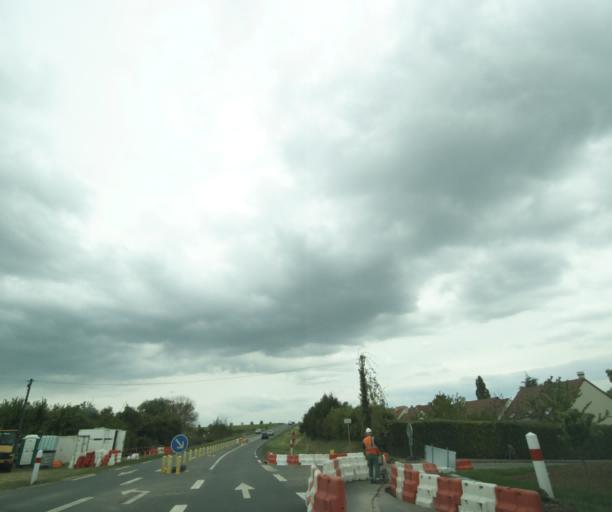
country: FR
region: Ile-de-France
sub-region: Departement des Yvelines
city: Ecquevilly
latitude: 48.9483
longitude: 1.9186
